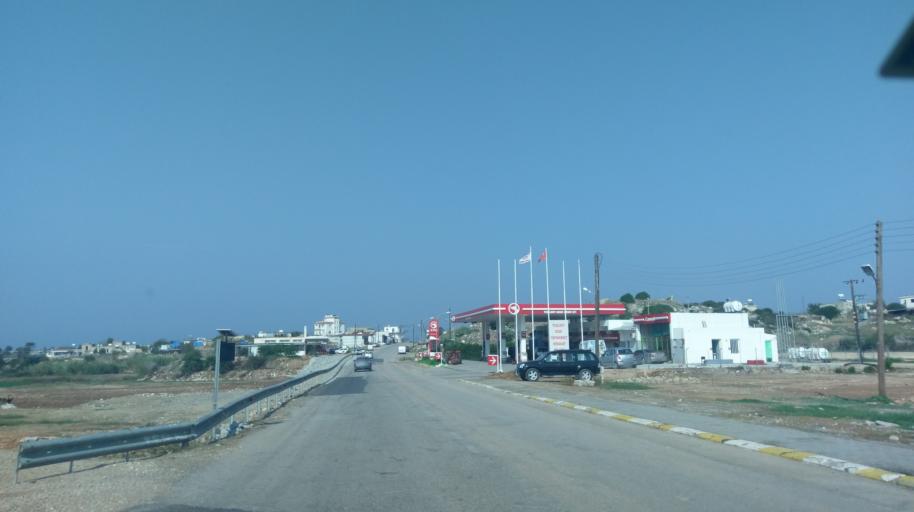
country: CY
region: Ammochostos
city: Leonarisso
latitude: 35.5054
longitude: 34.1612
